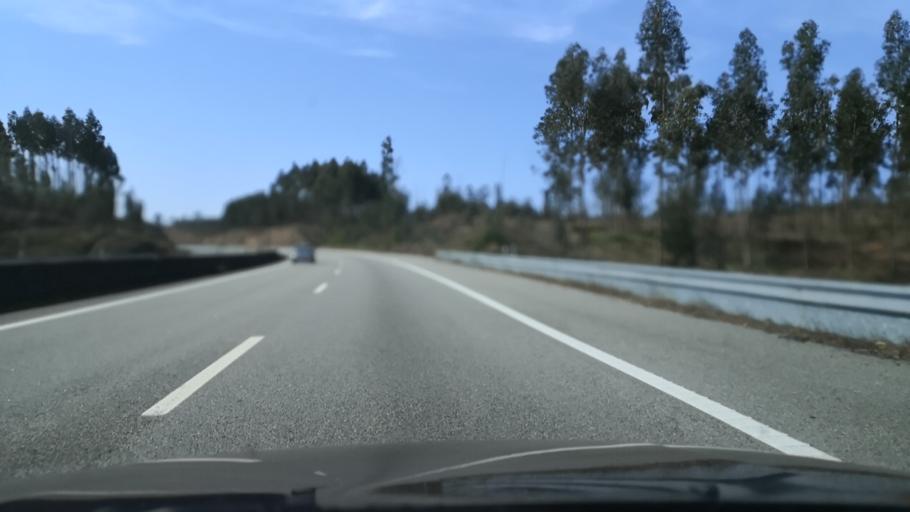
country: PT
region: Aveiro
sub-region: Agueda
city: Valongo
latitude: 40.6675
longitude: -8.4046
